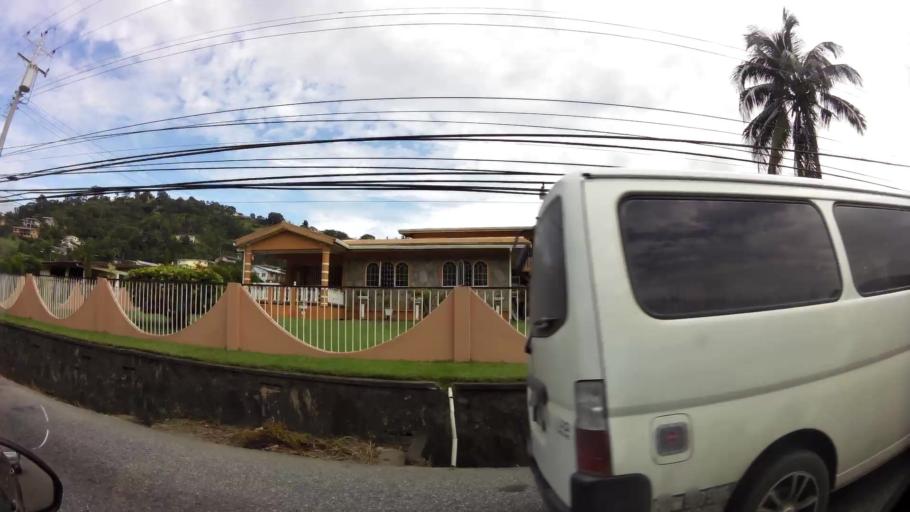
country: TT
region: San Juan/Laventille
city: Laventille
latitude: 10.6777
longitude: -61.4533
